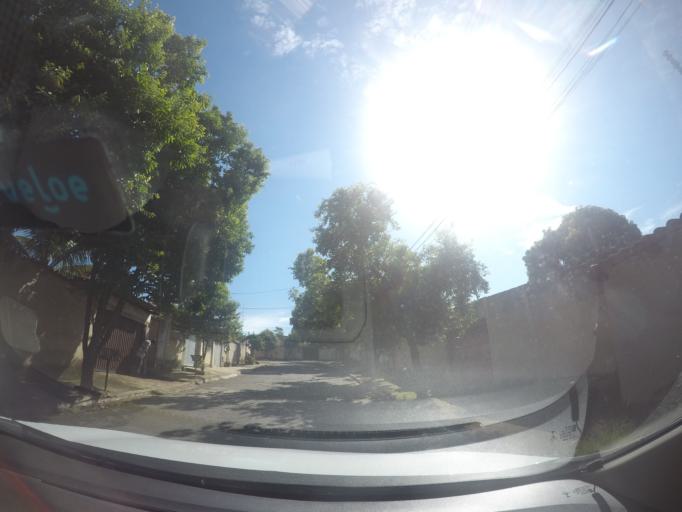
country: BR
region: Goias
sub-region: Goiania
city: Goiania
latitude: -16.6640
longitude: -49.1959
